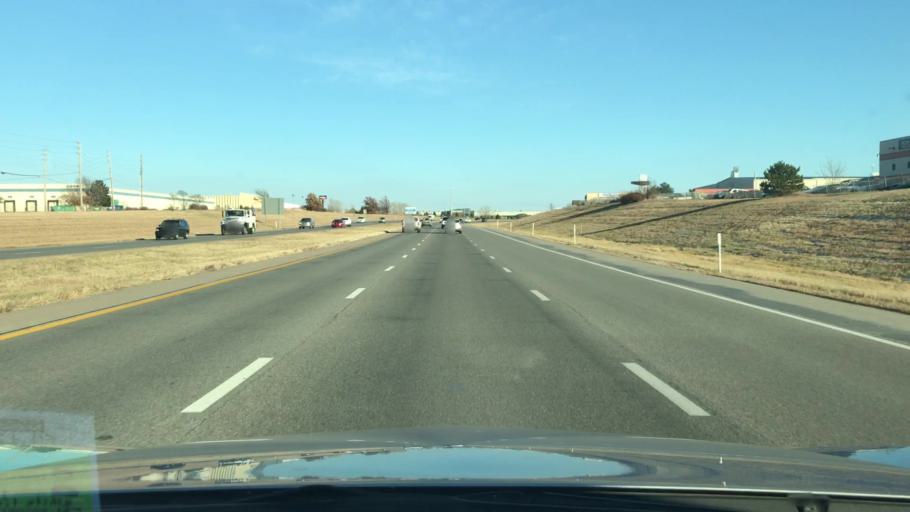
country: US
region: Kansas
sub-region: Sedgwick County
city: Bellaire
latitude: 37.7443
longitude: -97.2403
